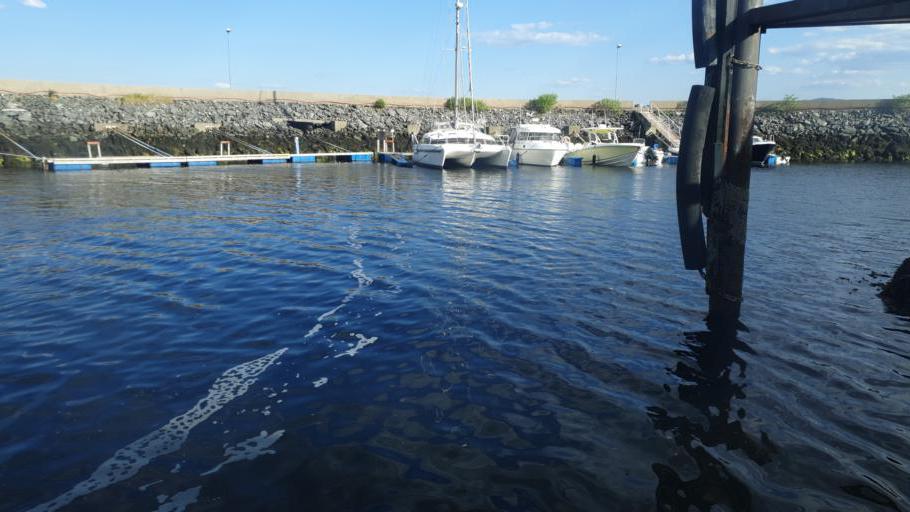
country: NO
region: Sor-Trondelag
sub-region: Trondheim
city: Trondheim
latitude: 63.5532
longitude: 10.2234
